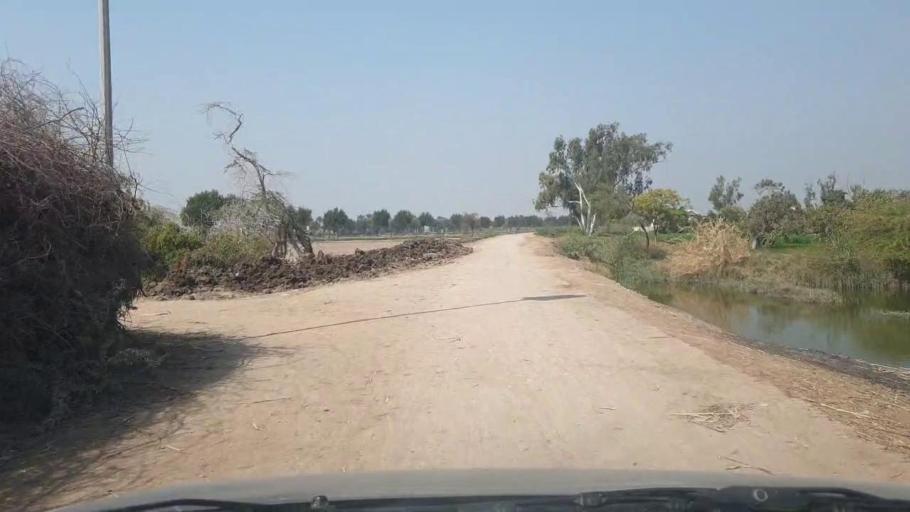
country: PK
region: Sindh
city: Mirwah Gorchani
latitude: 25.3574
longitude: 69.1450
